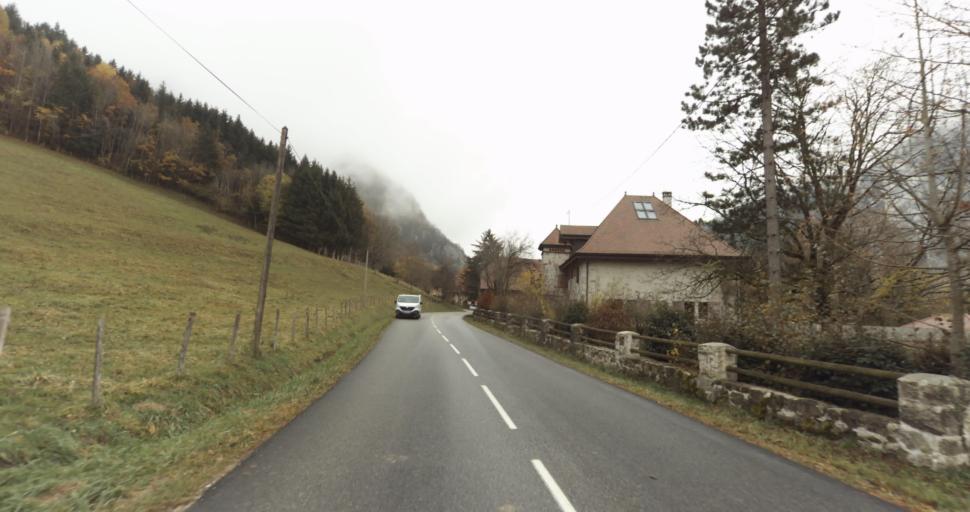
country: FR
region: Rhone-Alpes
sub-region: Departement de la Haute-Savoie
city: Thorens-Glieres
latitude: 45.9946
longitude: 6.2595
